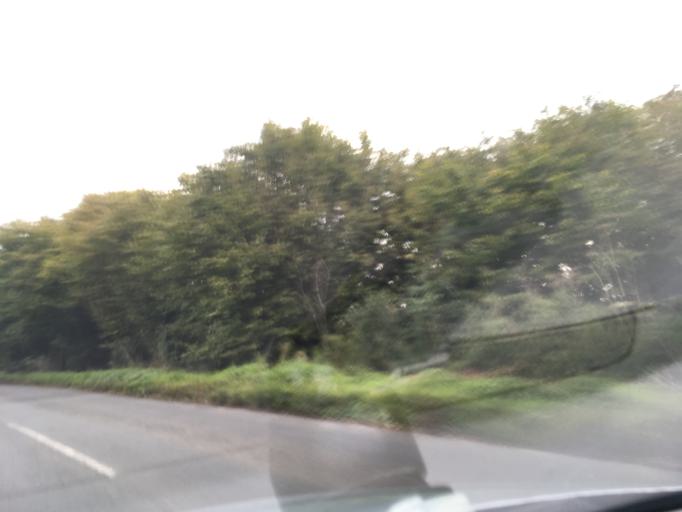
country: GB
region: England
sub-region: Oxfordshire
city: Cowley
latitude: 51.7701
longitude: -1.1908
